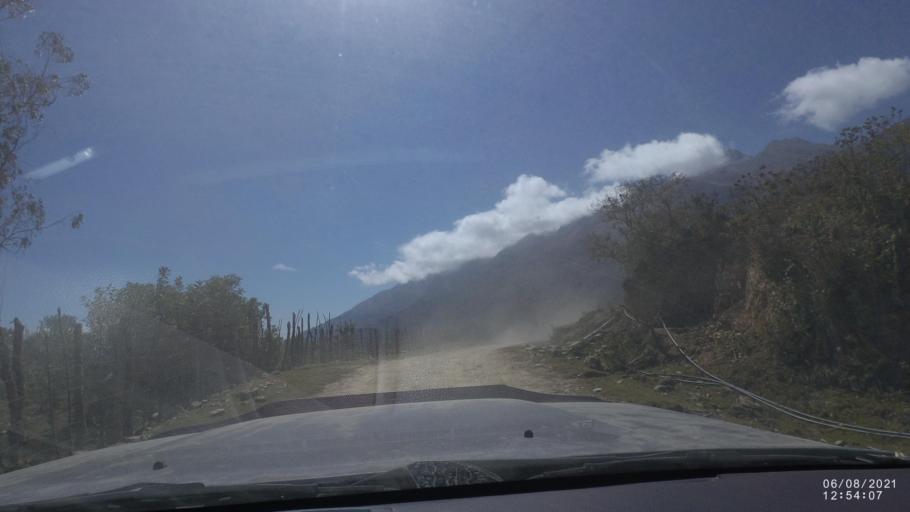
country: BO
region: Cochabamba
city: Colchani
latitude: -16.7596
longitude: -66.6838
